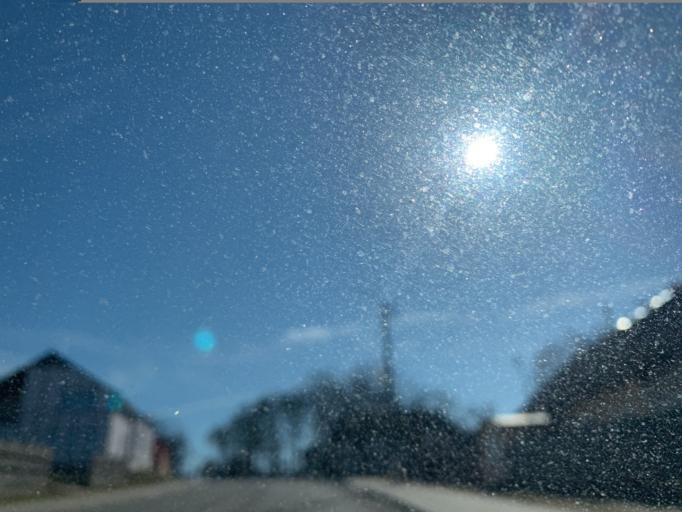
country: BY
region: Minsk
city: Nyasvizh
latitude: 53.2151
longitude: 26.6926
